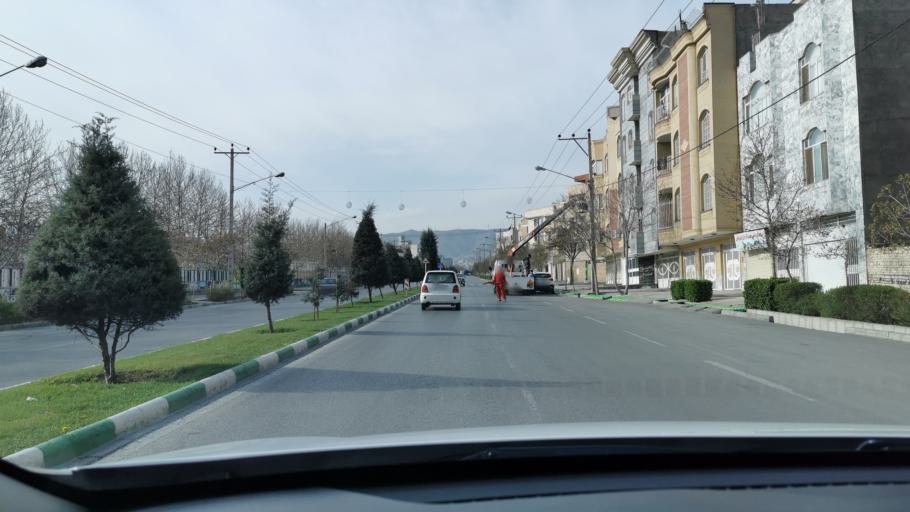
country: IR
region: Razavi Khorasan
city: Mashhad
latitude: 36.3092
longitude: 59.5151
